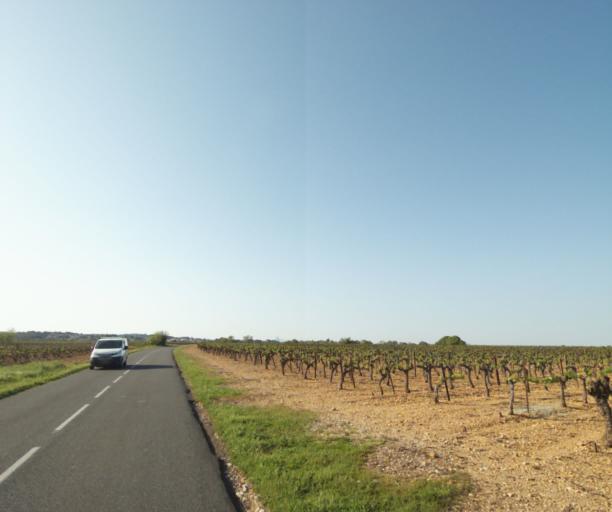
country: FR
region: Languedoc-Roussillon
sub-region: Departement de l'Herault
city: Laverune
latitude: 43.5973
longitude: 3.7932
